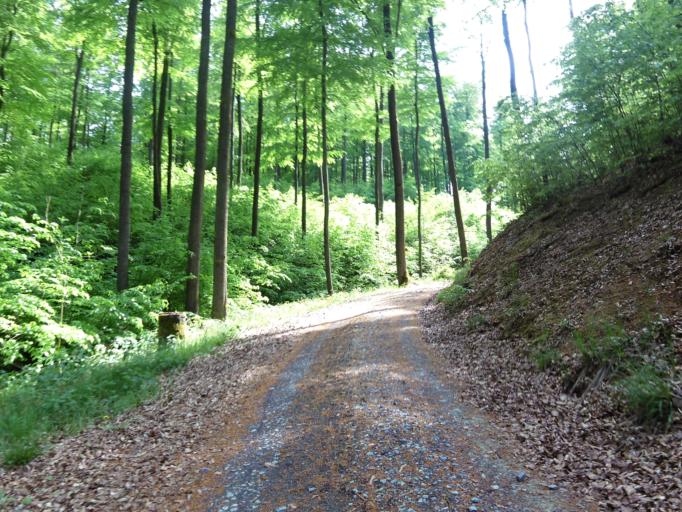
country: DE
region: Thuringia
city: Wolfsburg-Unkeroda
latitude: 50.9520
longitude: 10.2749
